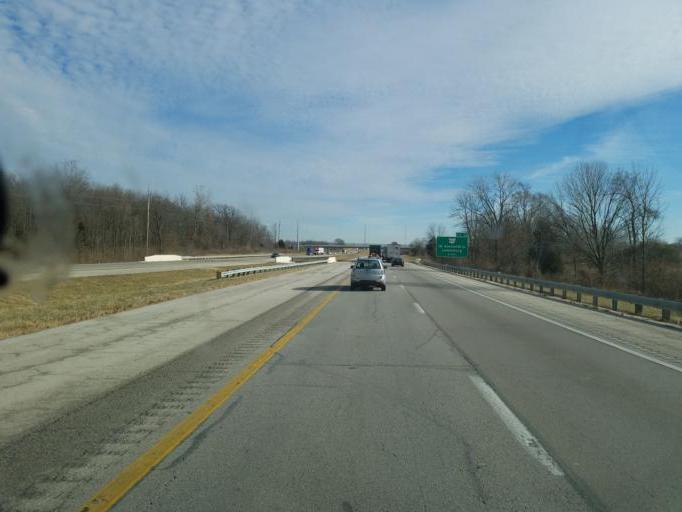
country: US
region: Ohio
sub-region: Preble County
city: Lewisburg
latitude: 39.8365
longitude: -84.5636
